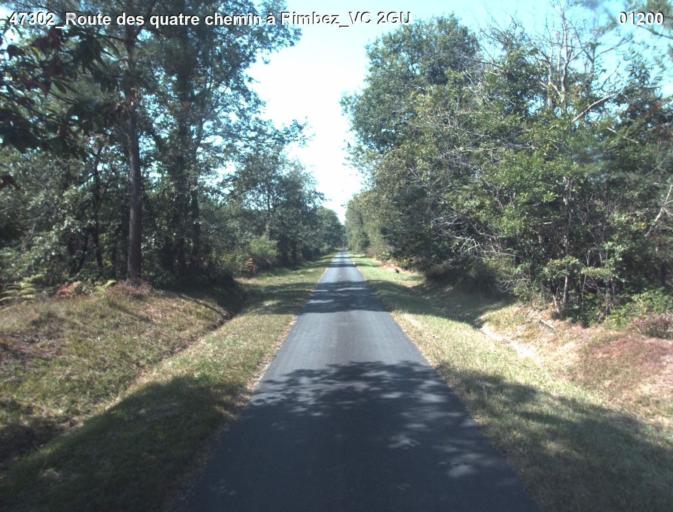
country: FR
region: Aquitaine
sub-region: Departement des Landes
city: Gabarret
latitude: 44.0320
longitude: 0.0805
